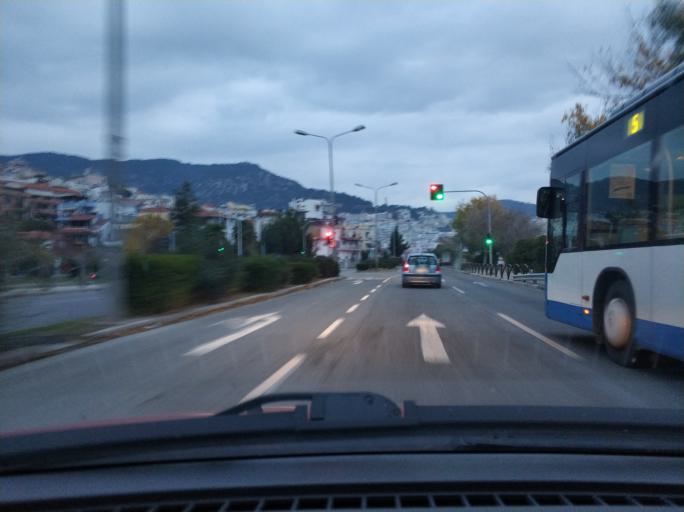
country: GR
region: East Macedonia and Thrace
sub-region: Nomos Kavalas
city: Kavala
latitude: 40.9308
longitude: 24.3918
